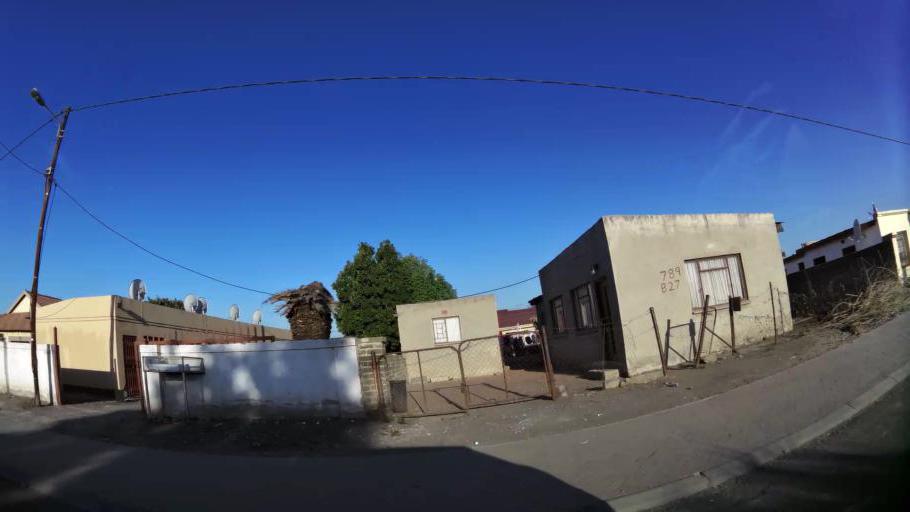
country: ZA
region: North-West
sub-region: Bojanala Platinum District Municipality
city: Rustenburg
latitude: -25.6366
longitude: 27.2196
